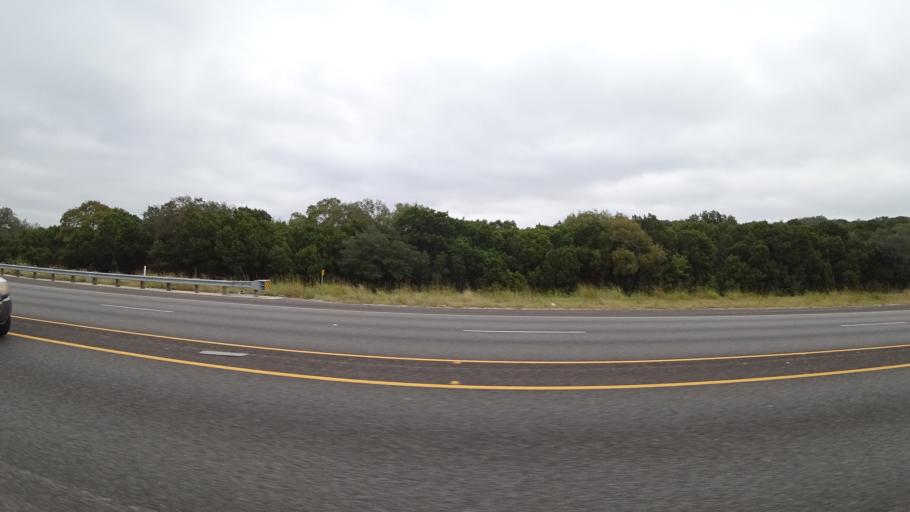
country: US
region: Texas
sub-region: Travis County
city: Barton Creek
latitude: 30.2667
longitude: -97.9093
